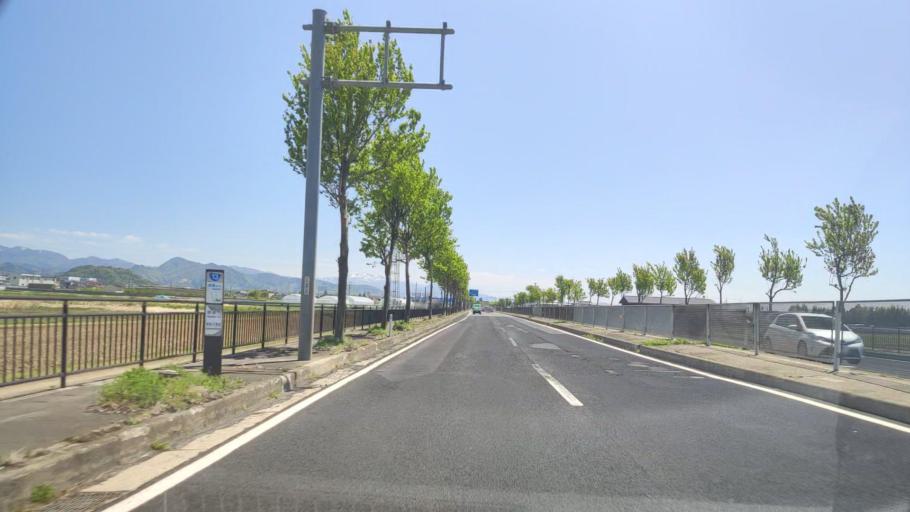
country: JP
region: Yamagata
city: Higashine
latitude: 38.4614
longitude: 140.3826
